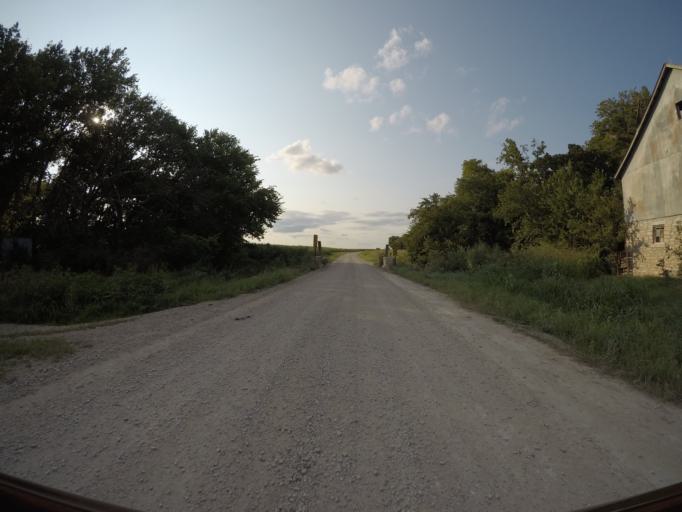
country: US
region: Kansas
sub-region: Wabaunsee County
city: Alma
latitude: 38.9262
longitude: -96.2271
